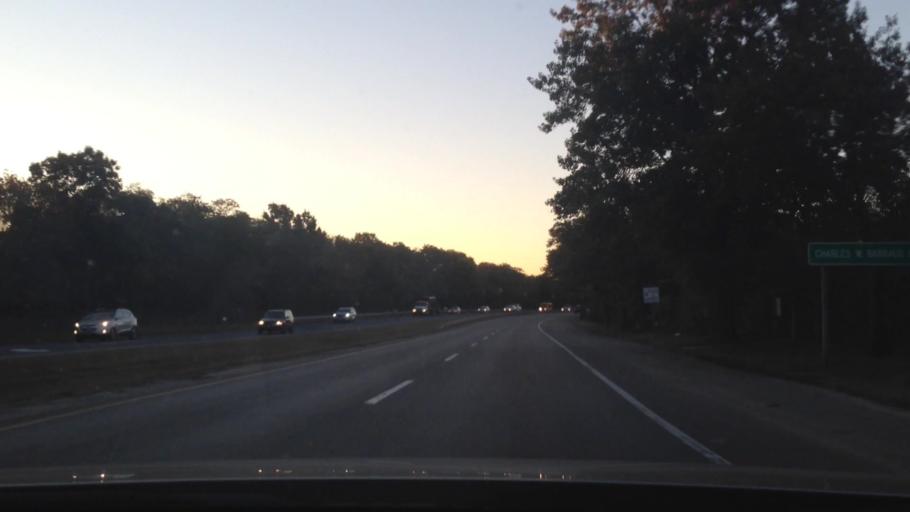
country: US
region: New York
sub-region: Suffolk County
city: Mount Sinai
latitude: 40.9373
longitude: -73.0108
